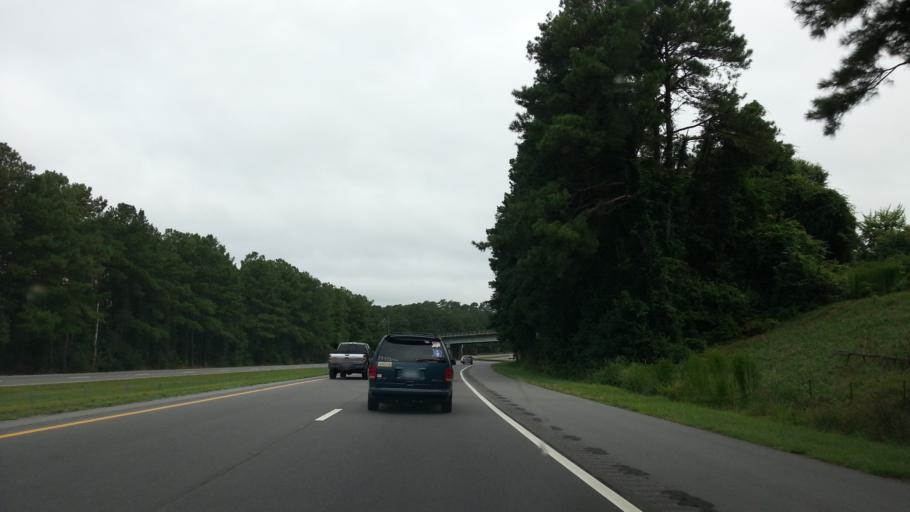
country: US
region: North Carolina
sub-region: Cumberland County
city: Fort Bragg
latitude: 35.0799
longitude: -78.9631
